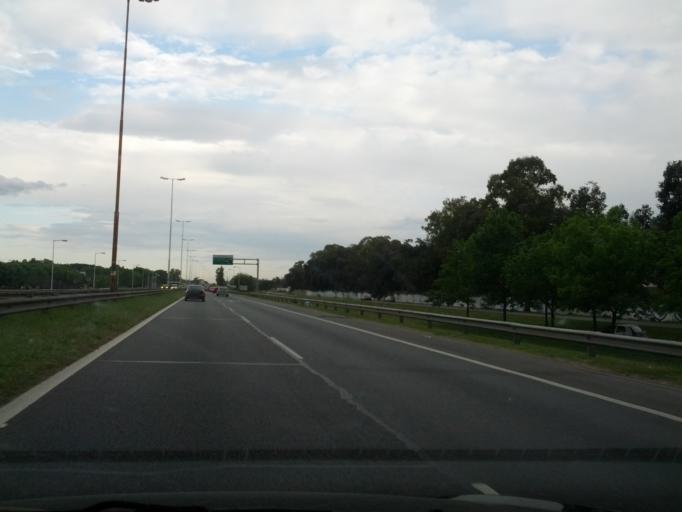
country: AR
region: Buenos Aires
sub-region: Partido de General Rodriguez
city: General Rodriguez
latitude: -34.5915
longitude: -58.9550
